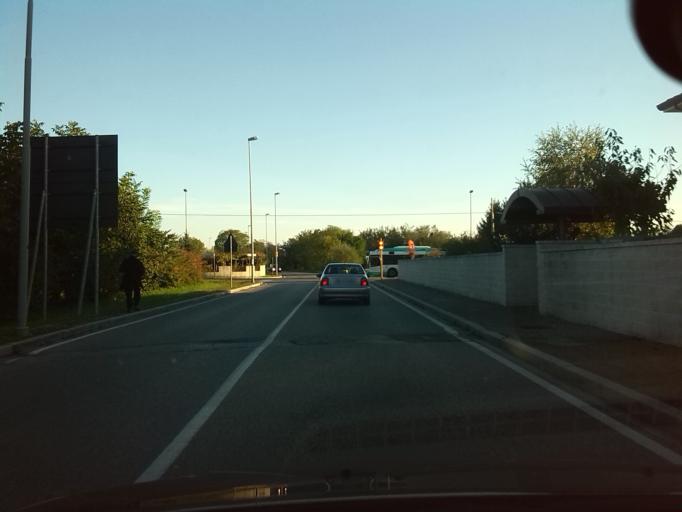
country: IT
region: Friuli Venezia Giulia
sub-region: Provincia di Udine
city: Passons
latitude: 46.0622
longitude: 13.2088
